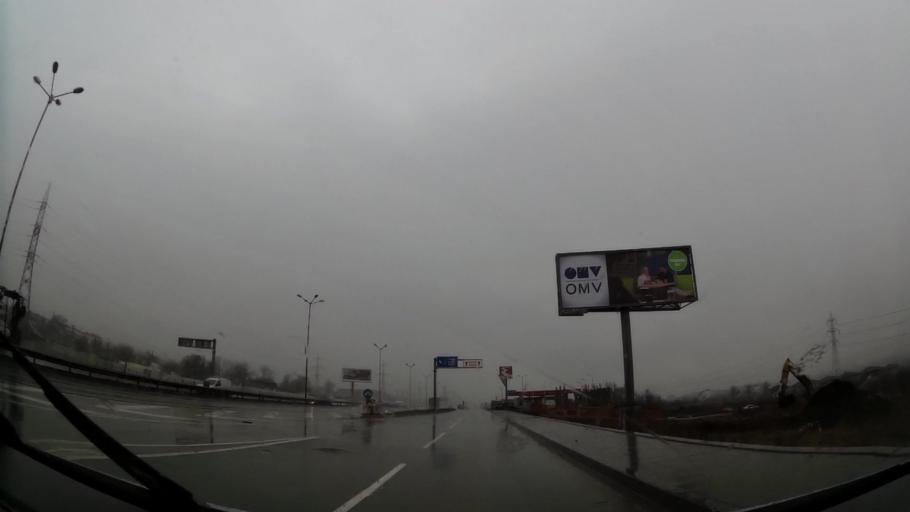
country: BG
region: Sofia-Capital
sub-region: Stolichna Obshtina
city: Sofia
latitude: 42.6276
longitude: 23.3474
